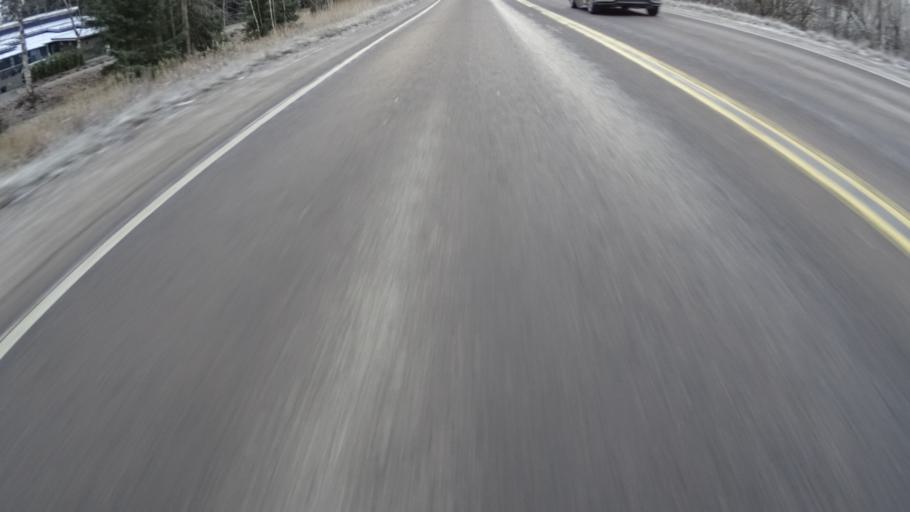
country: FI
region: Uusimaa
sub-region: Helsinki
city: Nurmijaervi
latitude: 60.4000
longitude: 24.7329
